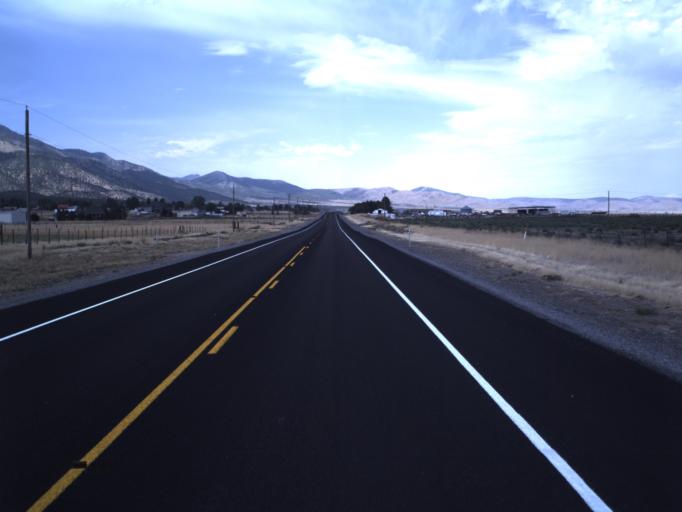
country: US
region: Utah
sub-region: Utah County
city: Eagle Mountain
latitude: 40.2877
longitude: -112.0970
